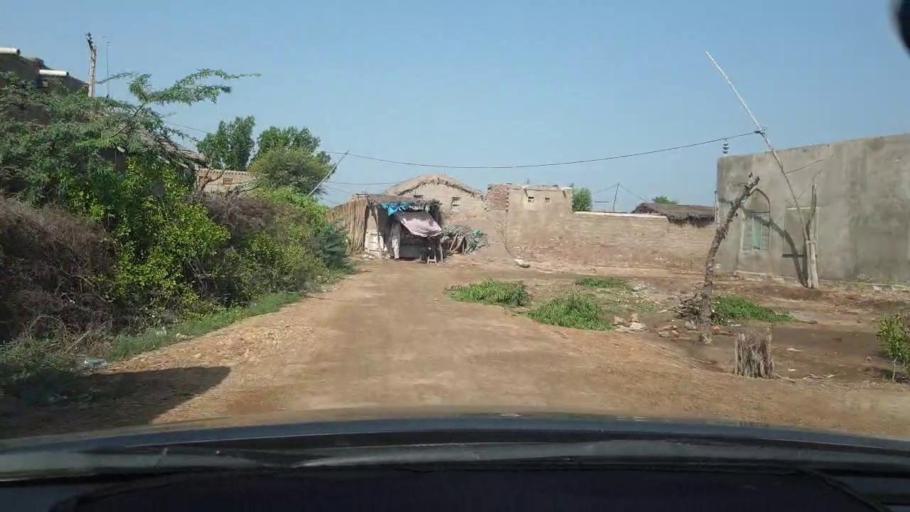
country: PK
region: Sindh
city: Tando Bago
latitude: 24.6885
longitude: 69.1227
